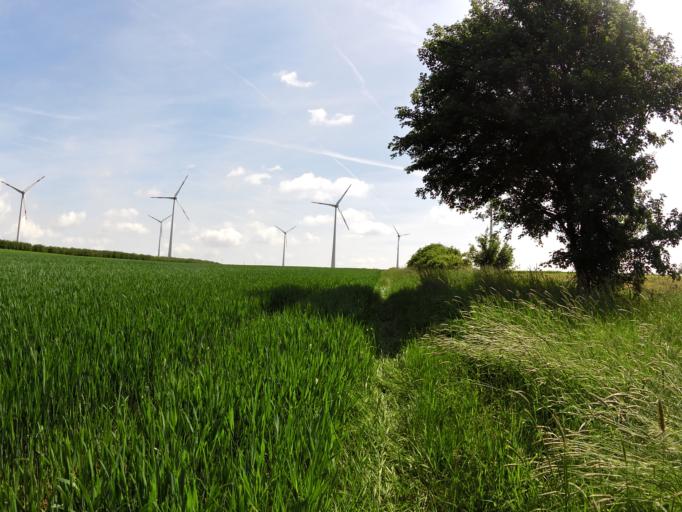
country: DE
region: Bavaria
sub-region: Regierungsbezirk Unterfranken
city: Sommerhausen
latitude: 49.7145
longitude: 10.0347
